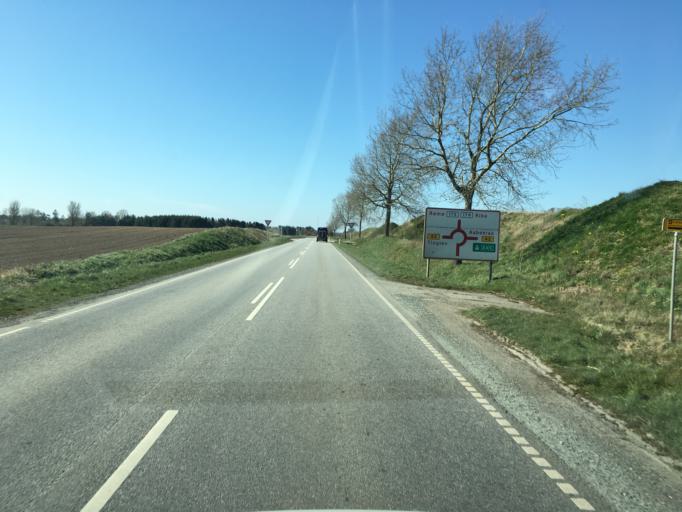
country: DK
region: South Denmark
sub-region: Aabenraa Kommune
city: Tinglev
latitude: 54.9690
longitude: 9.3139
